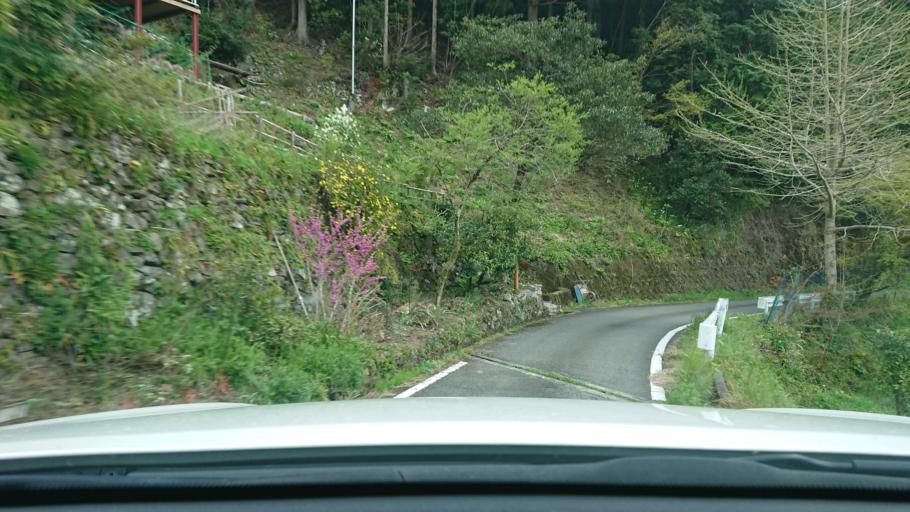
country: JP
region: Tokushima
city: Kamojimacho-jogejima
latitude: 33.8857
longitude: 134.3798
